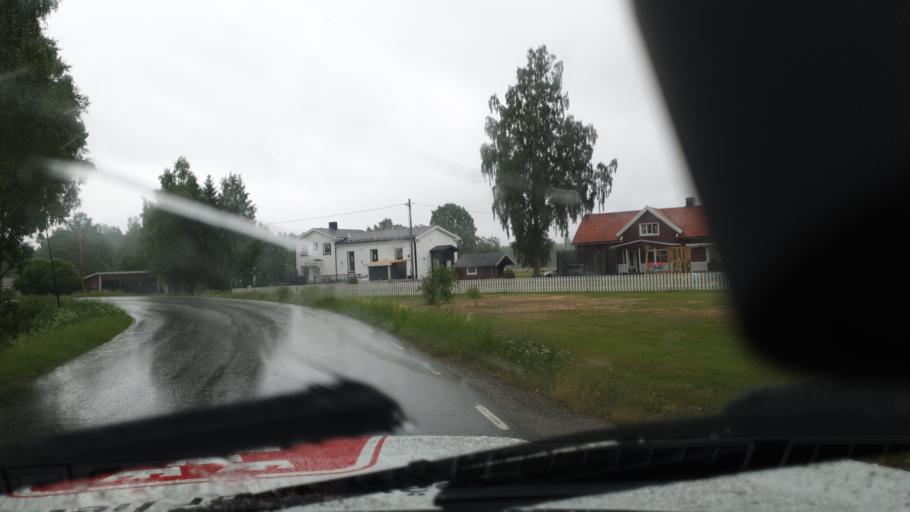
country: SE
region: Vaesterbotten
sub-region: Nordmalings Kommun
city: Nordmaling
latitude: 63.5471
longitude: 19.3934
